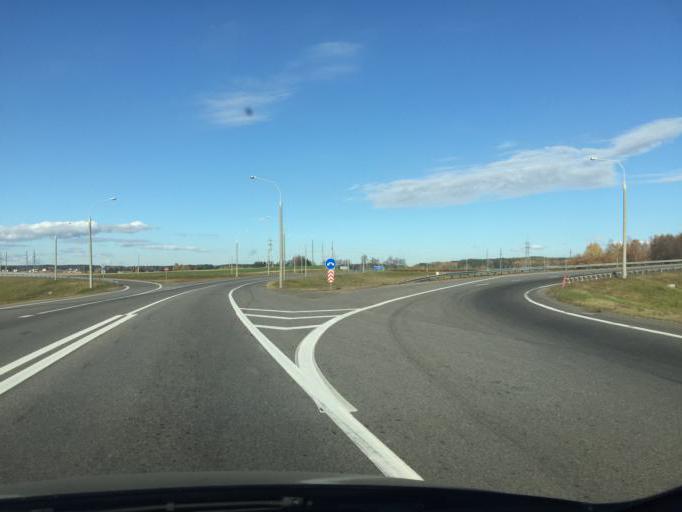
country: BY
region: Minsk
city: Slabada
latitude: 54.0164
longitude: 27.8906
